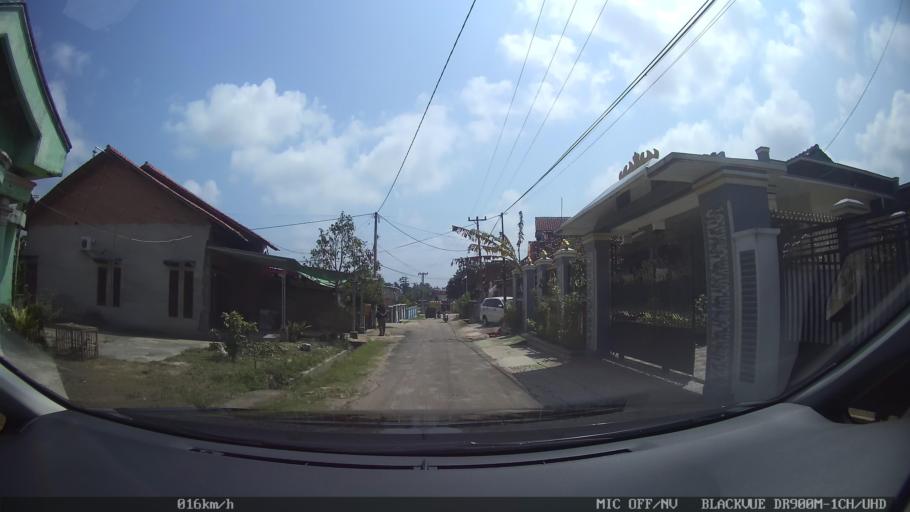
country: ID
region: Lampung
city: Kedaton
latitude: -5.3526
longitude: 105.2827
